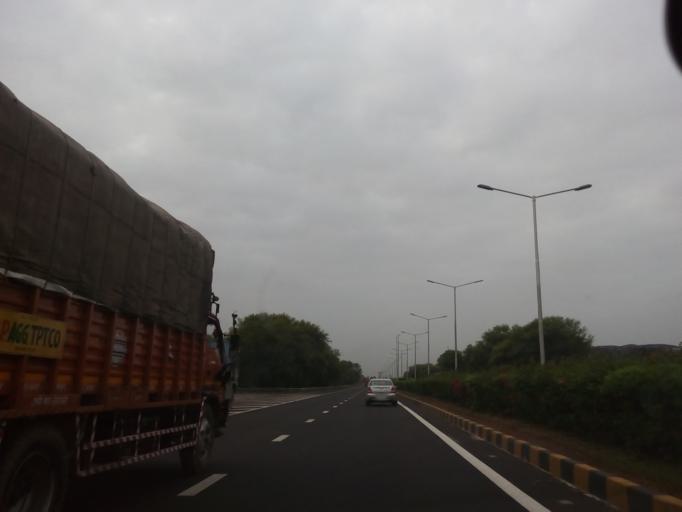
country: IN
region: Gujarat
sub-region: Anand
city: Anand
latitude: 22.5936
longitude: 72.9857
